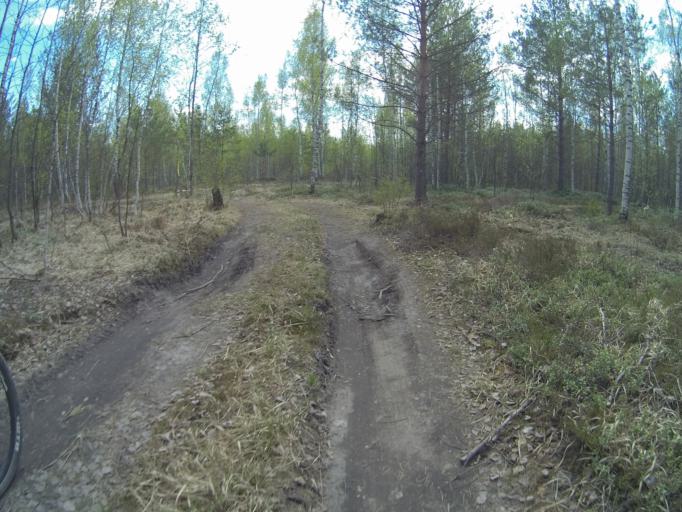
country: RU
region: Vladimir
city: Raduzhnyy
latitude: 55.9545
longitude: 40.2011
